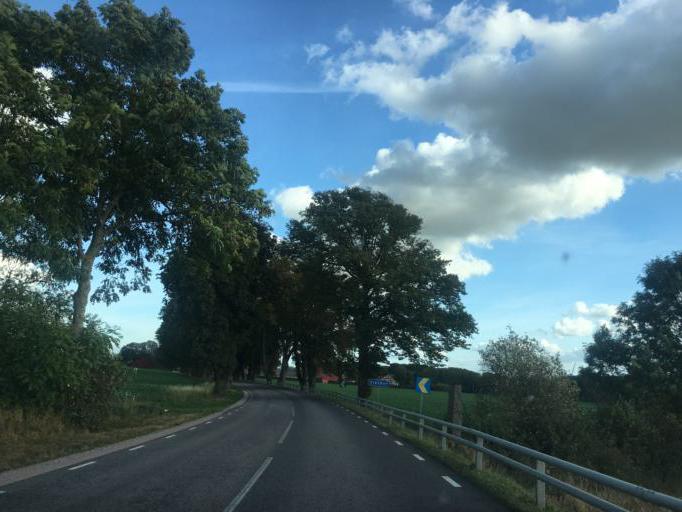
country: SE
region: Skane
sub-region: Eslovs Kommun
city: Eslov
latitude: 55.7819
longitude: 13.2769
